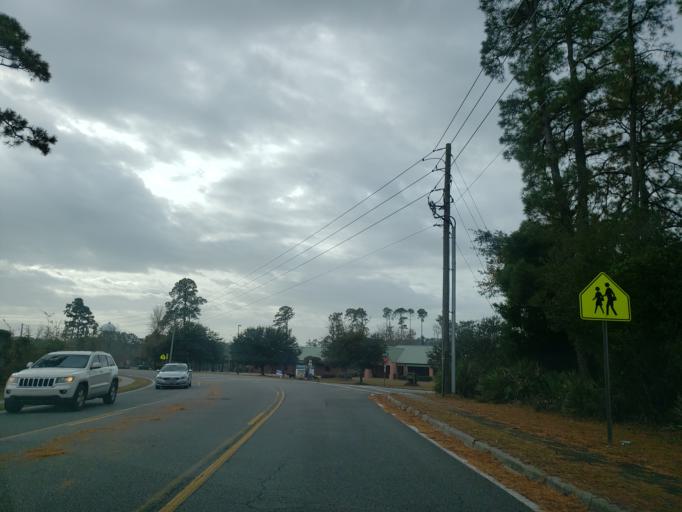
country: US
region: Georgia
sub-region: Chatham County
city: Whitemarsh Island
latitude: 32.0411
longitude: -81.0100
